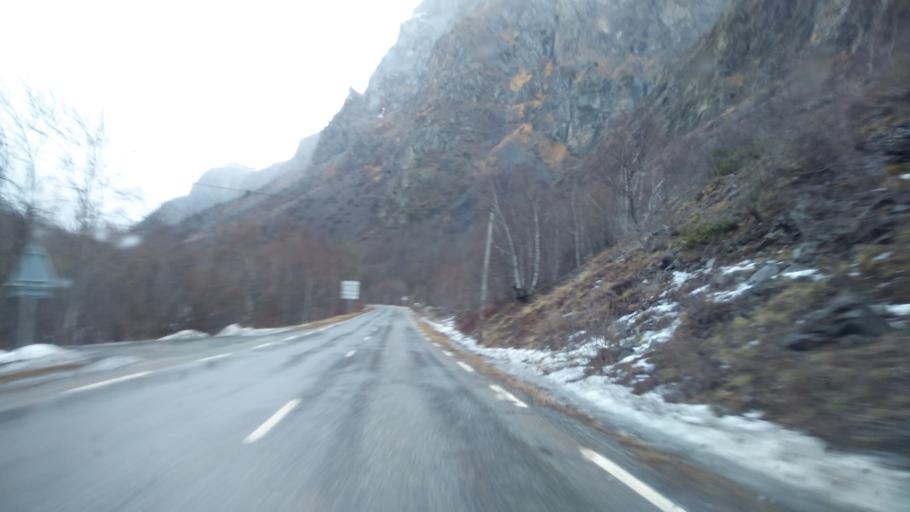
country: FR
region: Rhone-Alpes
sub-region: Departement de l'Isere
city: Mont-de-Lans
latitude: 45.0372
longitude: 6.2147
